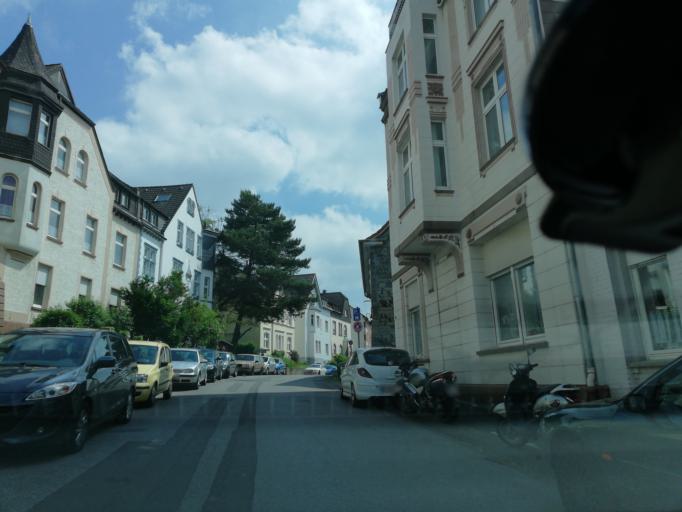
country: DE
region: North Rhine-Westphalia
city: Wetter (Ruhr)
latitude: 51.3898
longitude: 7.3935
